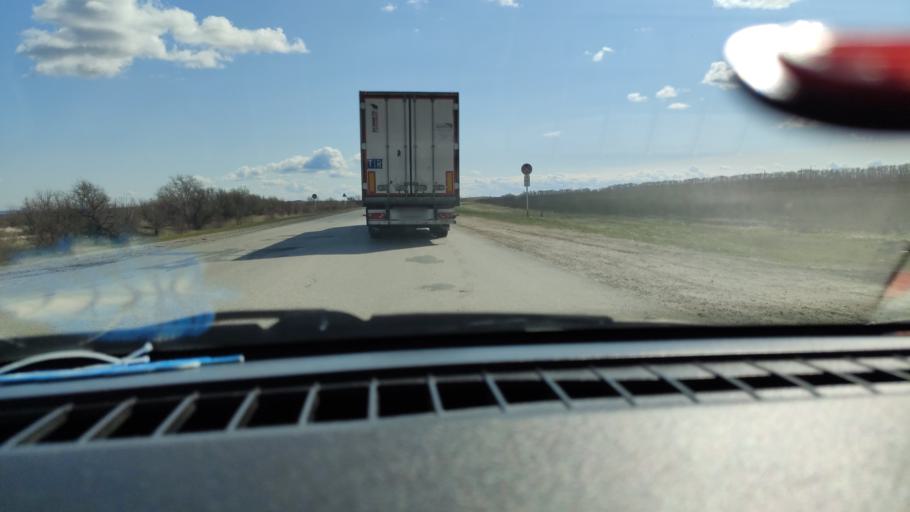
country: RU
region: Samara
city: Varlamovo
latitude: 53.1206
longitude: 48.3258
